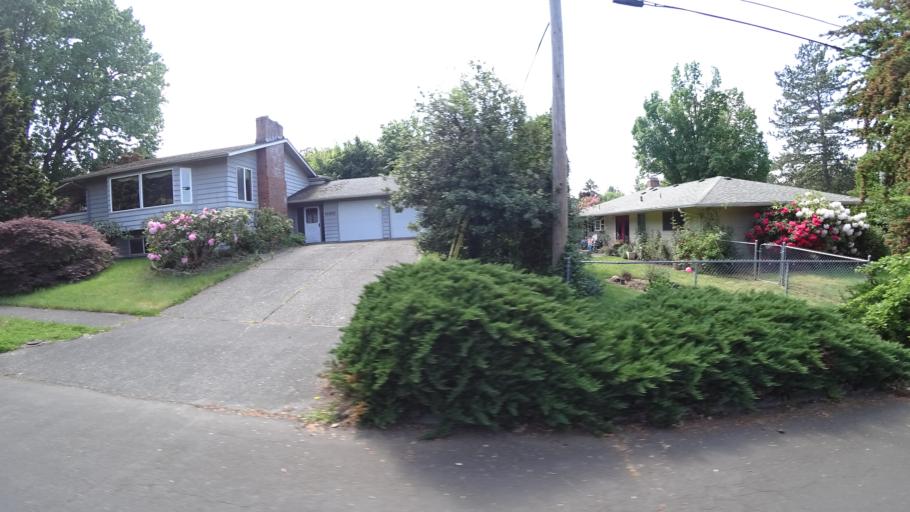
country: US
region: Oregon
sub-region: Washington County
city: Beaverton
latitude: 45.4662
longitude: -122.7948
